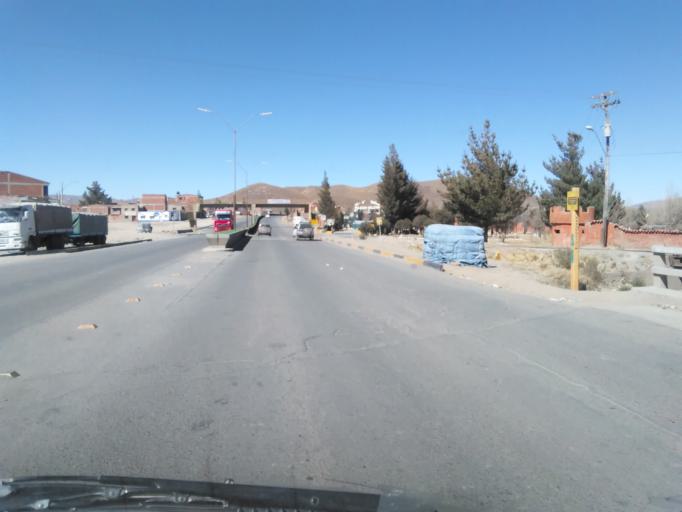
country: BO
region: Oruro
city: Oruro
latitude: -17.9784
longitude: -67.0558
